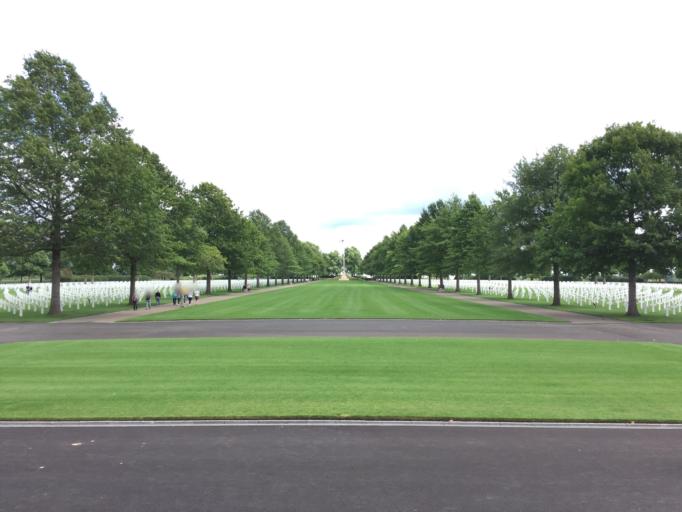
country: NL
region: Limburg
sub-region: Eijsden-Margraten
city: Margraten
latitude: 50.8176
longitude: 5.8046
